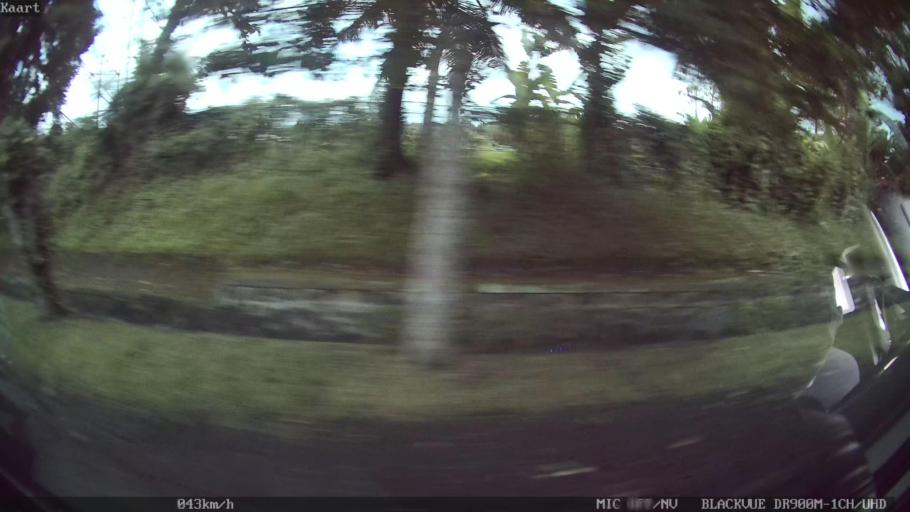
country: ID
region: Bali
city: Banjar Keraman
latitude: -8.5363
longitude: 115.2141
